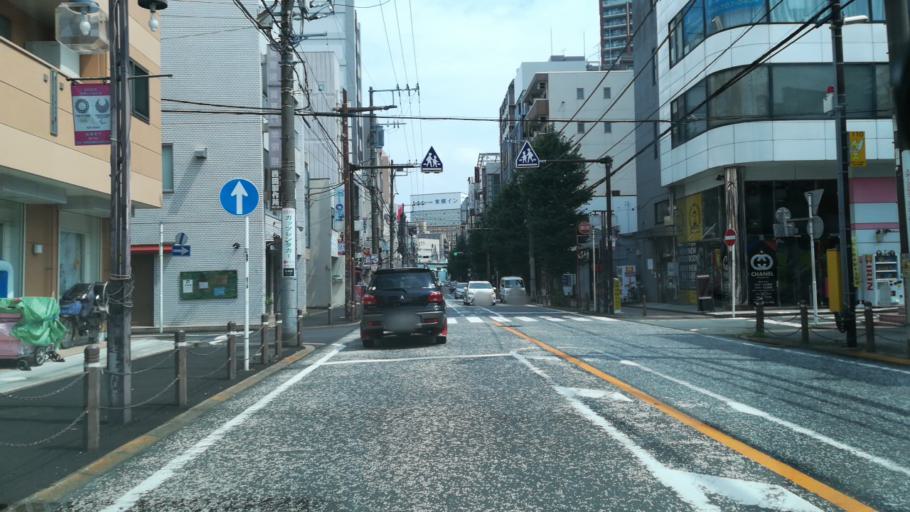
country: JP
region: Tokyo
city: Hachioji
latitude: 35.5811
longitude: 139.3682
